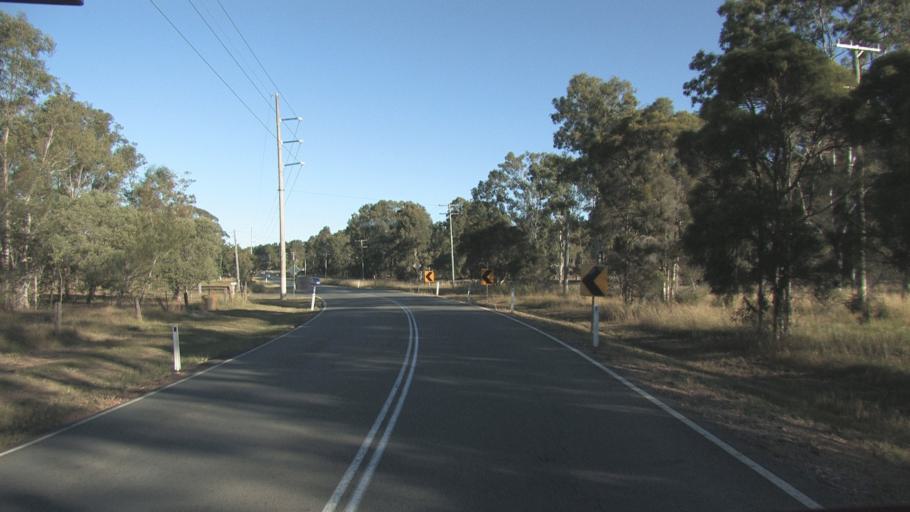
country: AU
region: Queensland
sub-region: Logan
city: Chambers Flat
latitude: -27.7401
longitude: 153.0869
